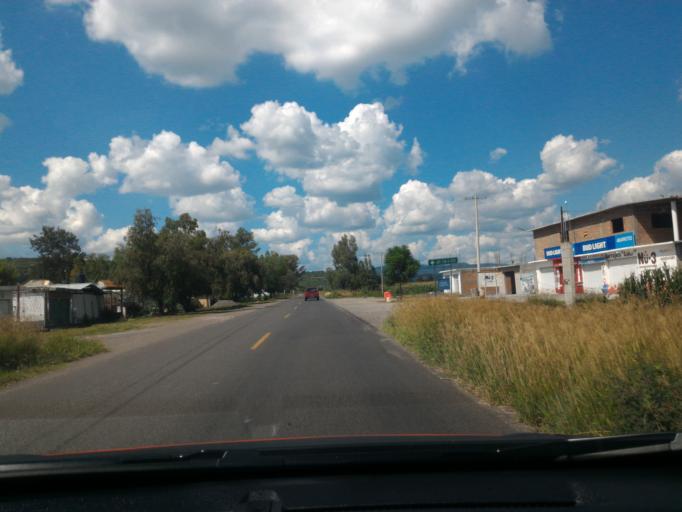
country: MX
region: Guanajuato
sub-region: Penjamo
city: Estacion la Piedad
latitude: 20.4715
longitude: -101.9772
